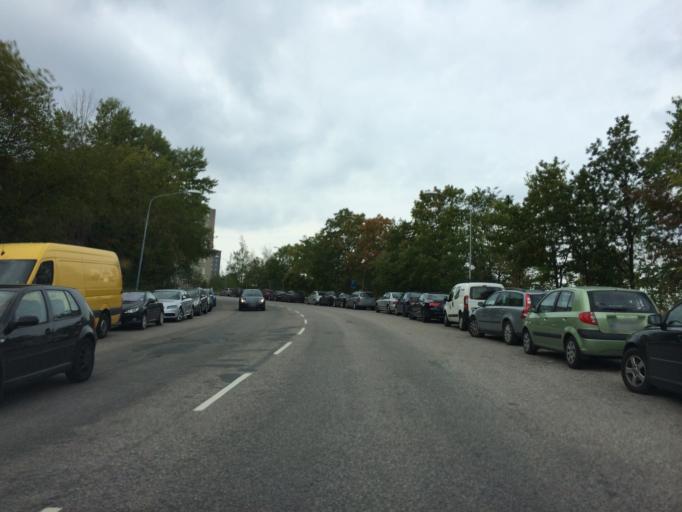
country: SE
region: Stockholm
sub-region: Stockholms Kommun
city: Arsta
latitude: 59.3092
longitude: 18.0188
